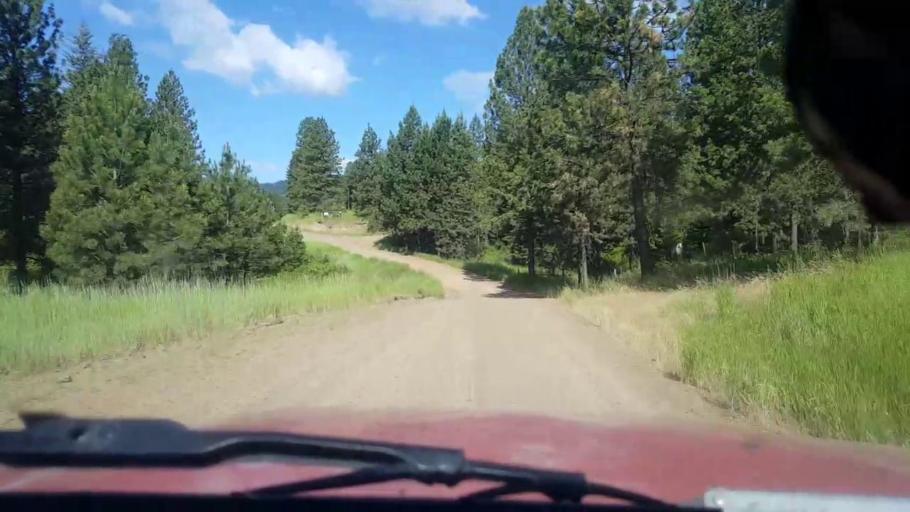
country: US
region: Washington
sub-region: Garfield County
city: Pomeroy
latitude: 46.0370
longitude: -117.4268
